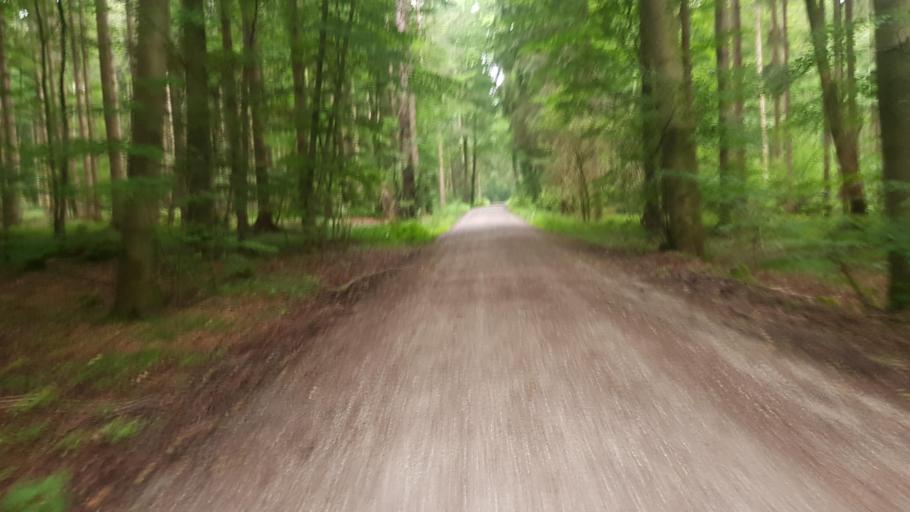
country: DE
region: Bavaria
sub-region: Upper Bavaria
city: Gauting
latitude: 48.0417
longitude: 11.3483
